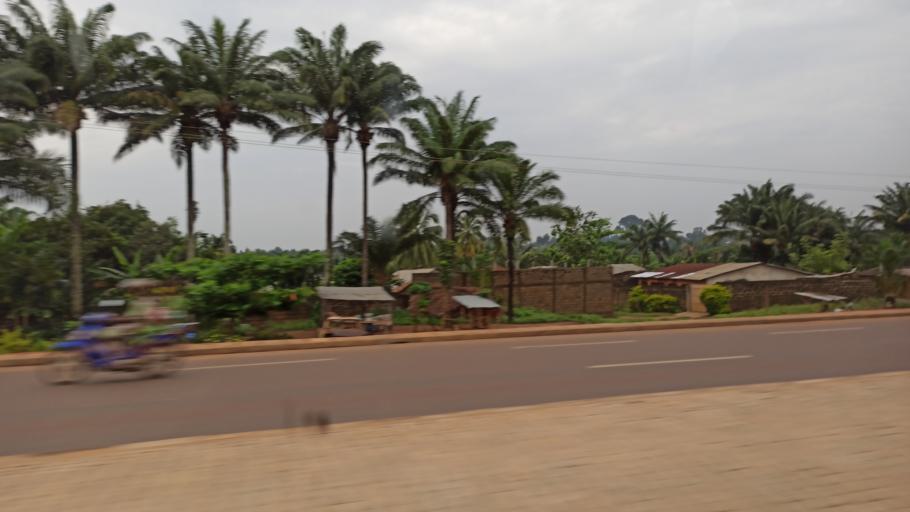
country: BJ
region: Queme
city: Porto-Novo
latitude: 6.5292
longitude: 2.6003
